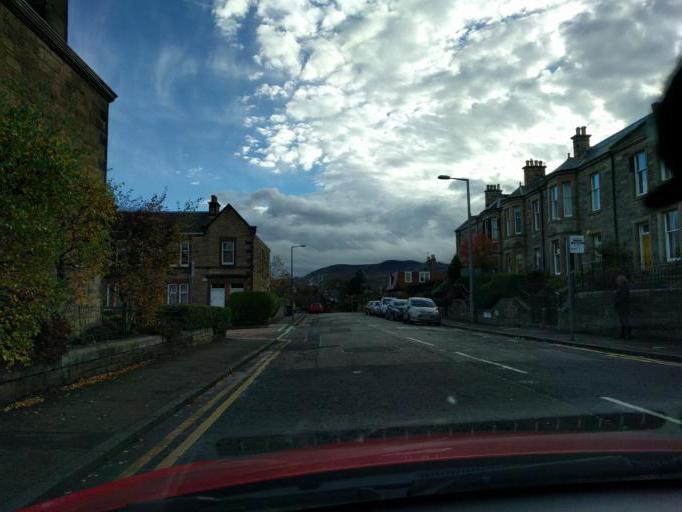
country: GB
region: Scotland
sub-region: Edinburgh
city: Colinton
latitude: 55.9212
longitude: -3.2216
